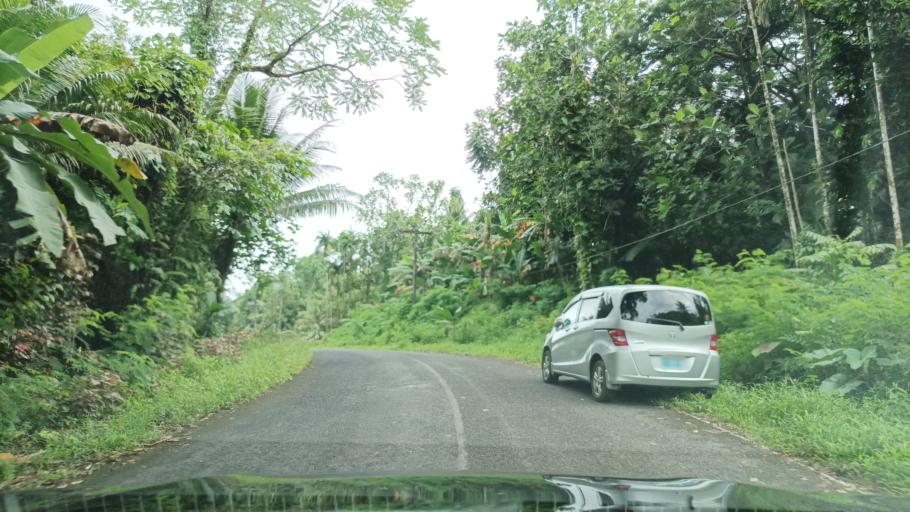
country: FM
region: Pohnpei
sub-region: Madolenihm Municipality
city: Madolenihm Municipality Government
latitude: 6.8307
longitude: 158.2977
